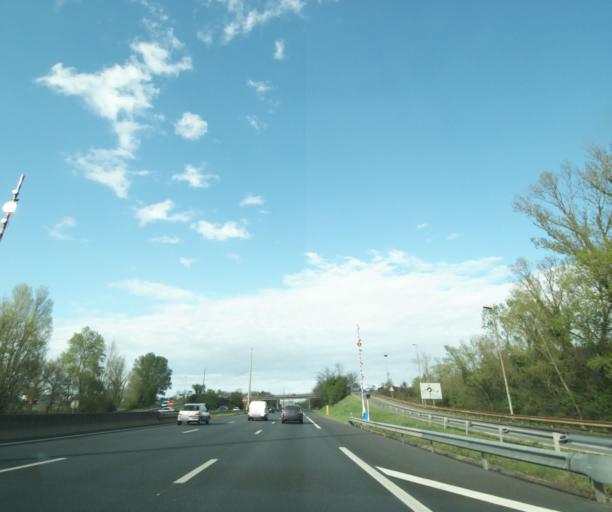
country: FR
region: Rhone-Alpes
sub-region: Departement du Rhone
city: Serezin-du-Rhone
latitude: 45.6408
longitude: 4.8262
